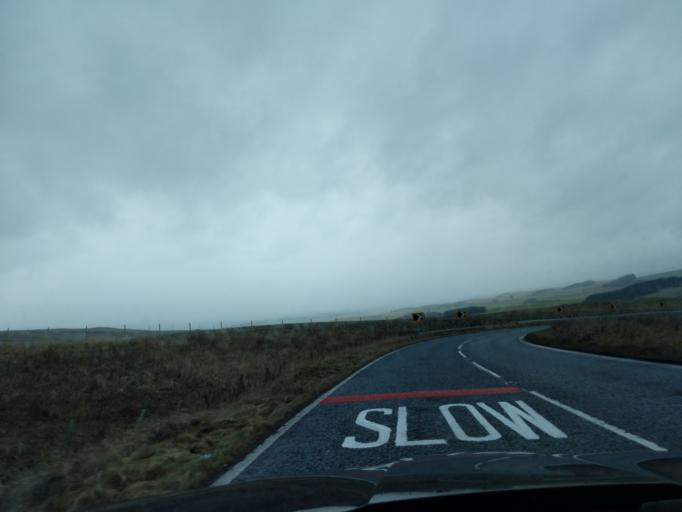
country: GB
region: England
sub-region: Northumberland
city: Otterburn
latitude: 55.2122
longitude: -2.1092
